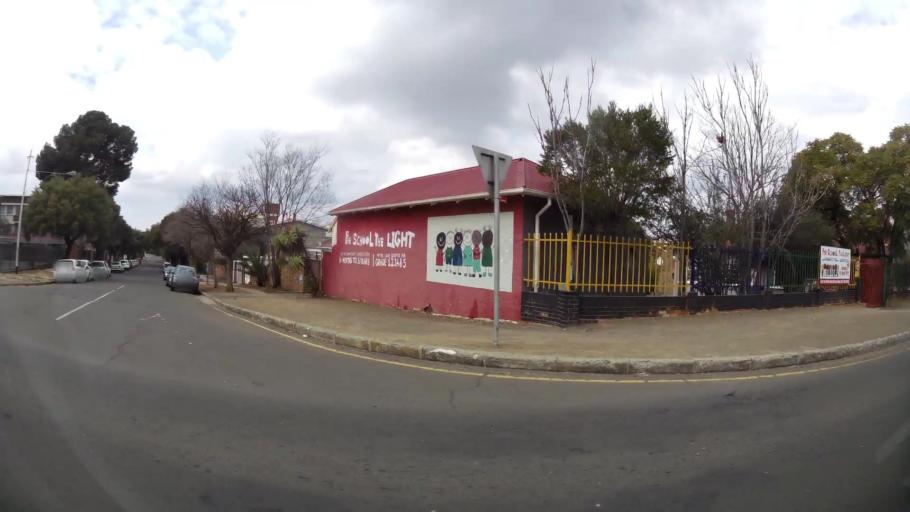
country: ZA
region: Orange Free State
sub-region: Mangaung Metropolitan Municipality
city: Bloemfontein
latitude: -29.1089
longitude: 26.2176
